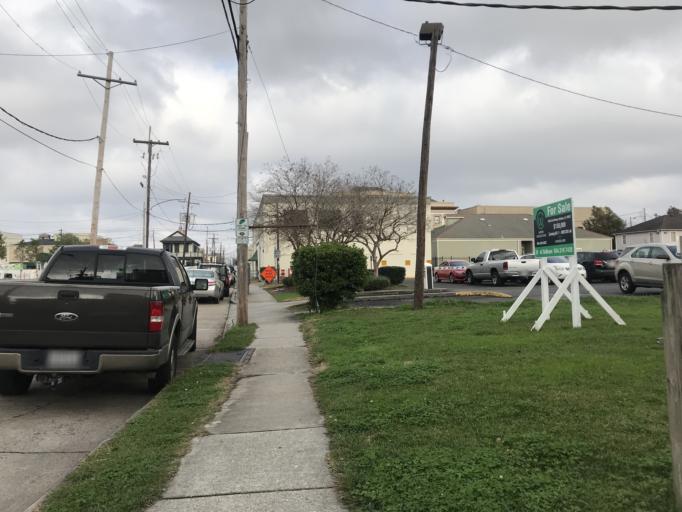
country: US
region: Louisiana
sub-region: Jefferson Parish
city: Gretna
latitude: 29.9165
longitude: -90.0668
